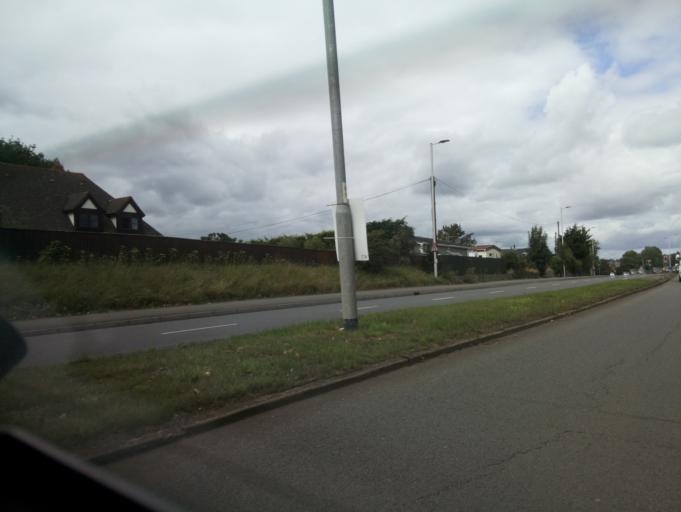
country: GB
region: England
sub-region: Devon
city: Heavitree
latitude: 50.7207
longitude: -3.4791
